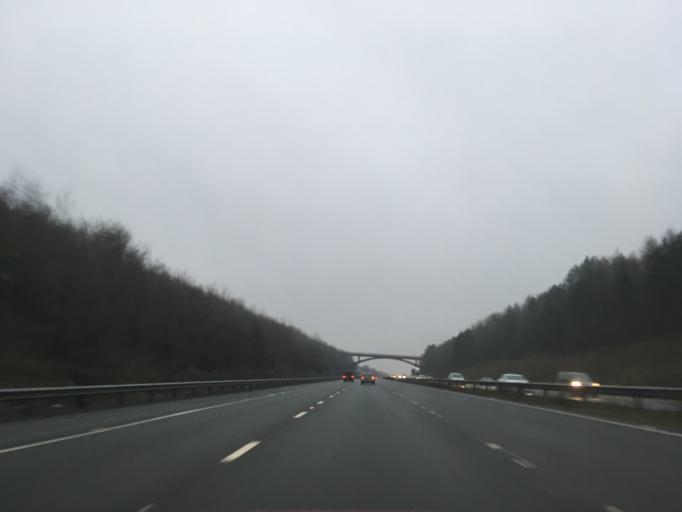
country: GB
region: Wales
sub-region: Caerphilly County Borough
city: Caerphilly
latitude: 51.5468
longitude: -3.1817
